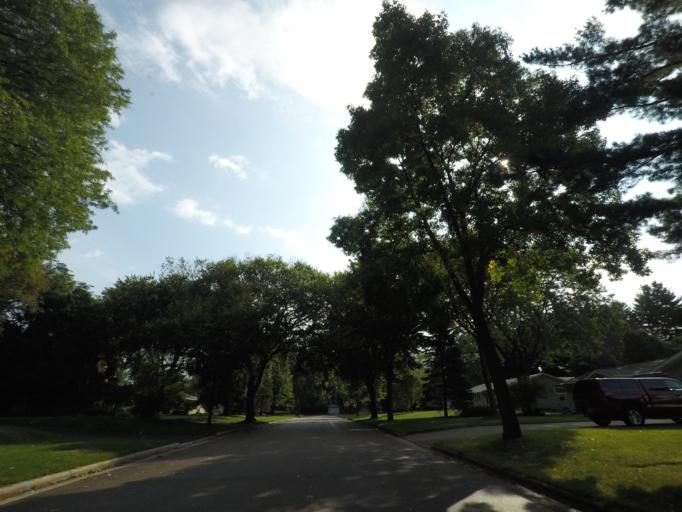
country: US
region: Wisconsin
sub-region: Dane County
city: Shorewood Hills
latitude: 43.0380
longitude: -89.4659
